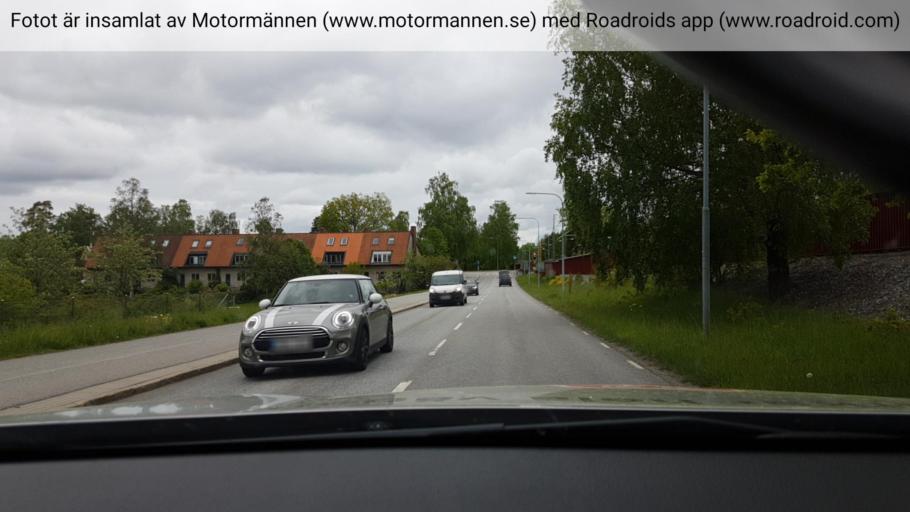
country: SE
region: Stockholm
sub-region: Lidingo
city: Brevik
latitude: 59.3470
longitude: 18.1994
